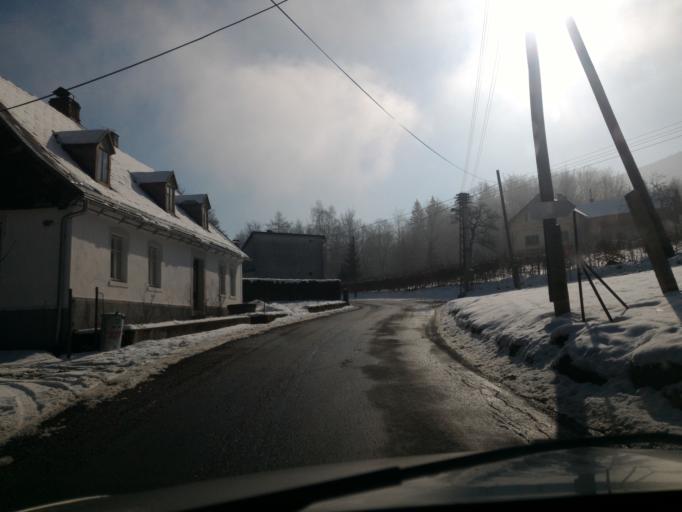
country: CZ
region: Liberecky
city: Nove Mesto pod Smrkem
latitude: 50.8708
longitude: 15.2361
